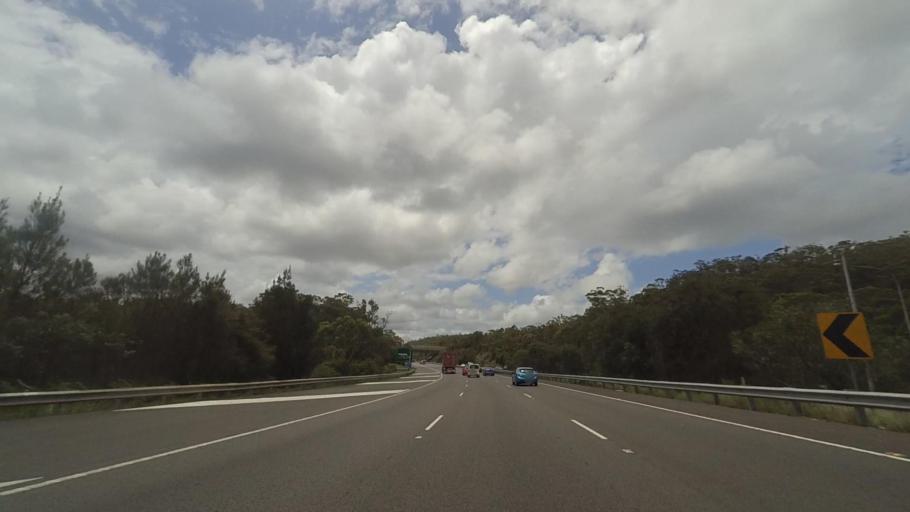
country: AU
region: New South Wales
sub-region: Gosford Shire
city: Point Clare
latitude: -33.4477
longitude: 151.2182
